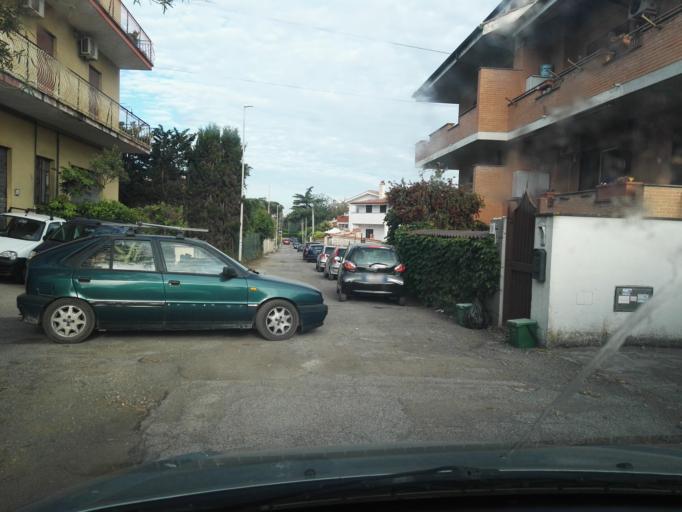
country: IT
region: Latium
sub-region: Citta metropolitana di Roma Capitale
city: Selcetta
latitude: 41.7703
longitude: 12.4817
